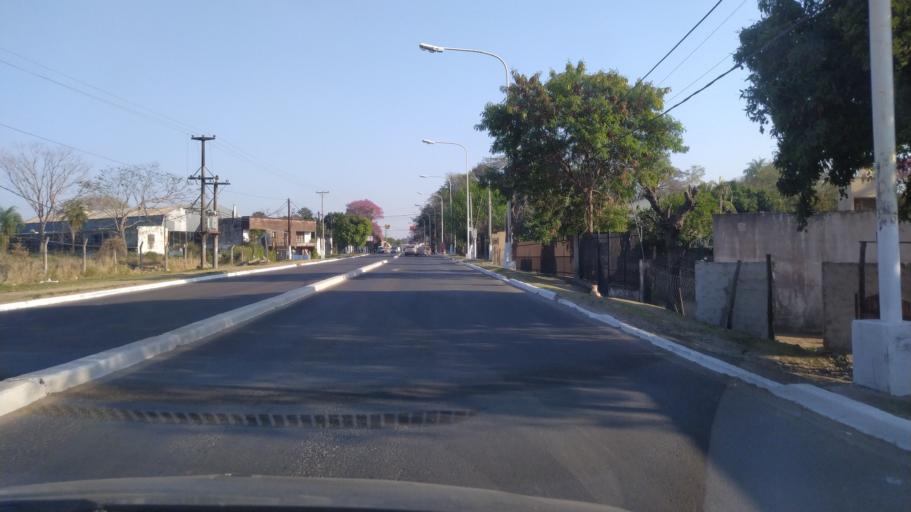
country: AR
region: Corrientes
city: Corrientes
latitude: -27.5146
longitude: -58.8062
